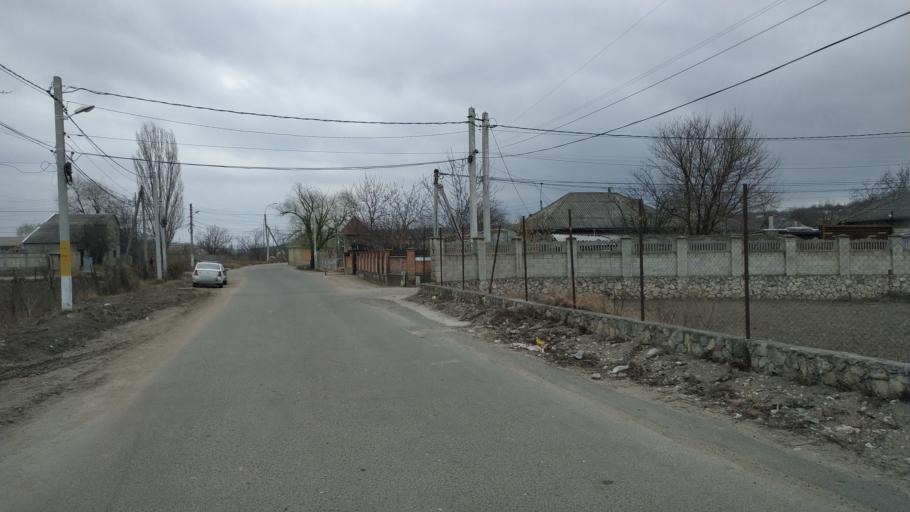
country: MD
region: Laloveni
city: Ialoveni
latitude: 46.9387
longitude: 28.7731
